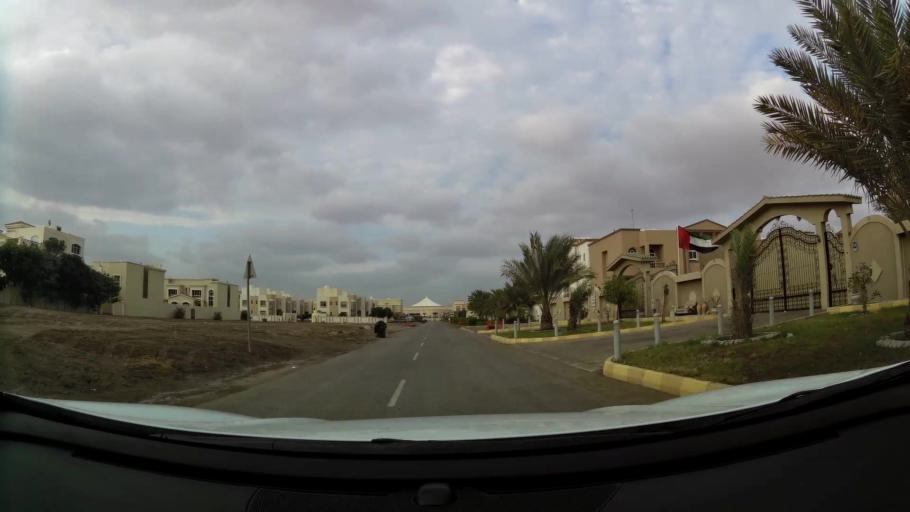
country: AE
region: Abu Dhabi
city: Abu Dhabi
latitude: 24.3571
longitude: 54.5529
